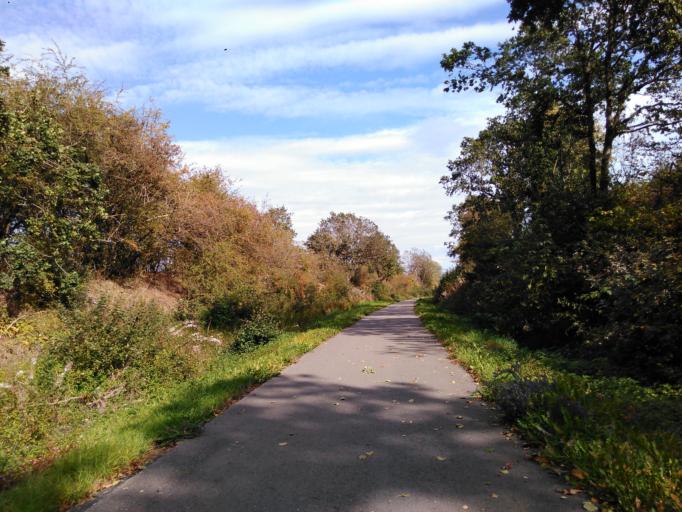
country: BE
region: Wallonia
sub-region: Province du Luxembourg
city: Gouvy
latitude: 50.1579
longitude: 5.9349
